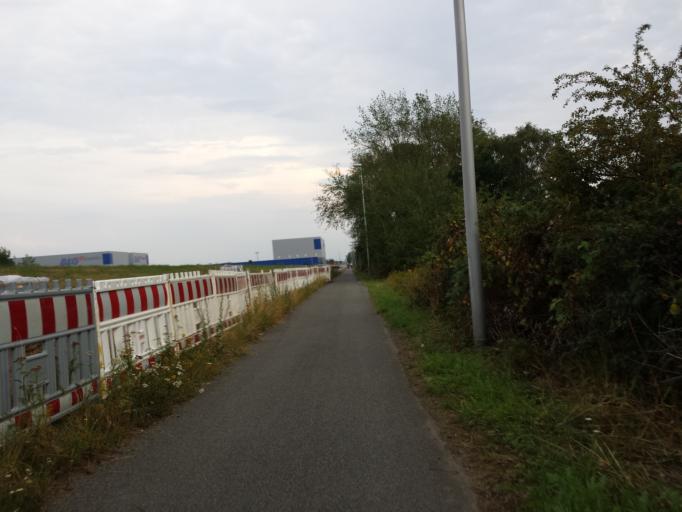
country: DE
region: Lower Saxony
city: Stuhr
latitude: 53.0962
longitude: 8.7282
